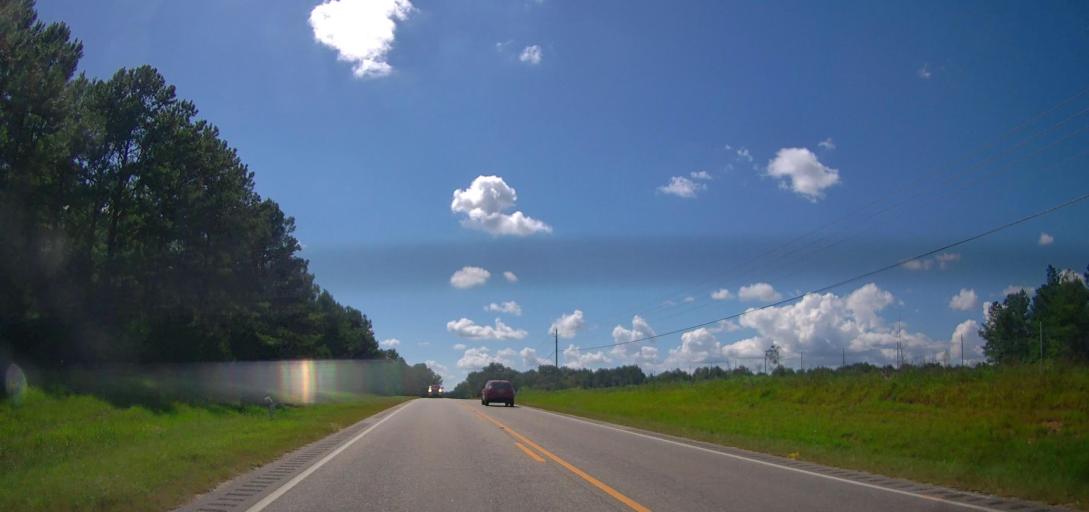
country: US
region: Alabama
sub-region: Macon County
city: Tuskegee
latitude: 32.3811
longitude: -85.8002
